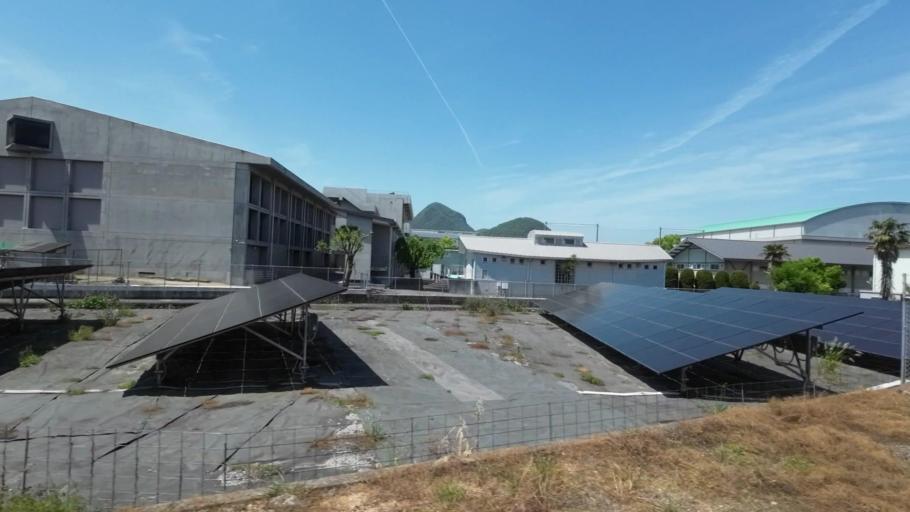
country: JP
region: Kagawa
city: Marugame
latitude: 34.2291
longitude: 133.7897
